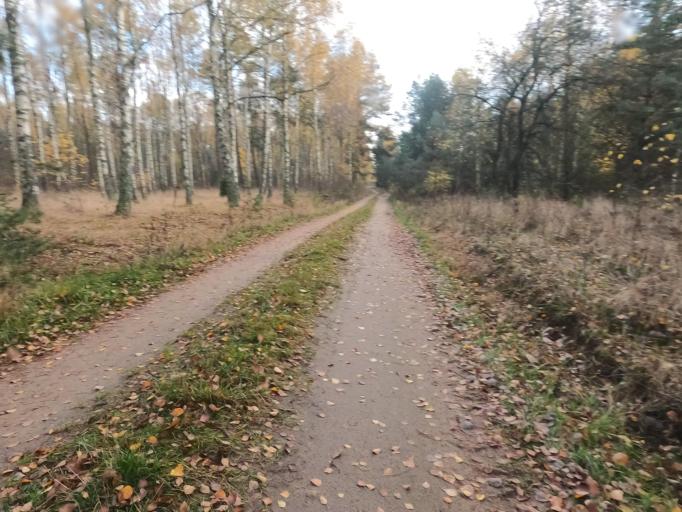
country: PL
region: West Pomeranian Voivodeship
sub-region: Powiat szczecinecki
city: Lubowo
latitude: 53.5435
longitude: 16.4331
